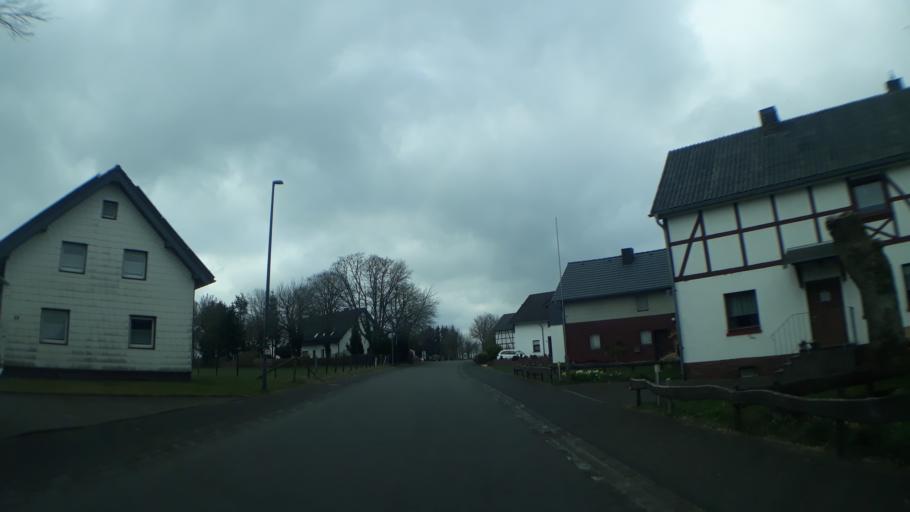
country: DE
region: North Rhine-Westphalia
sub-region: Regierungsbezirk Koln
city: Hellenthal
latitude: 50.5419
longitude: 6.4033
